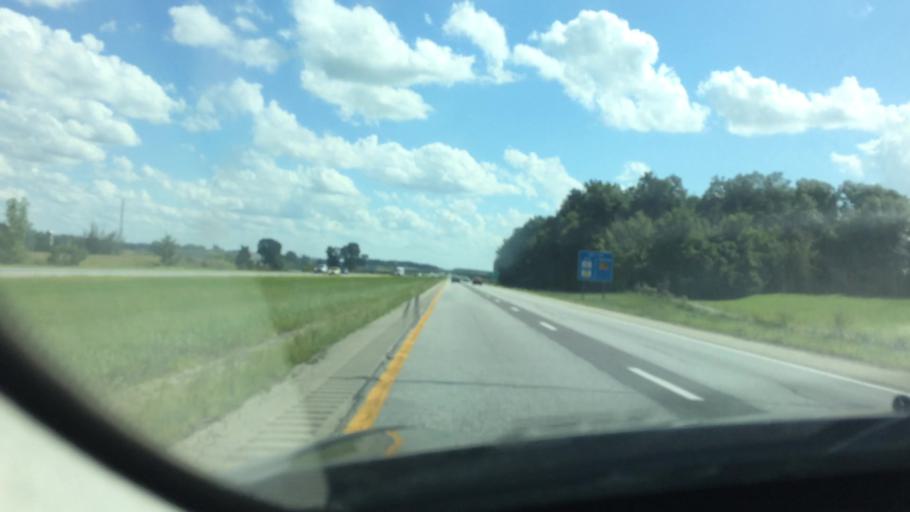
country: US
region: Ohio
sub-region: Shelby County
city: Botkins
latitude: 40.4766
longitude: -84.1694
